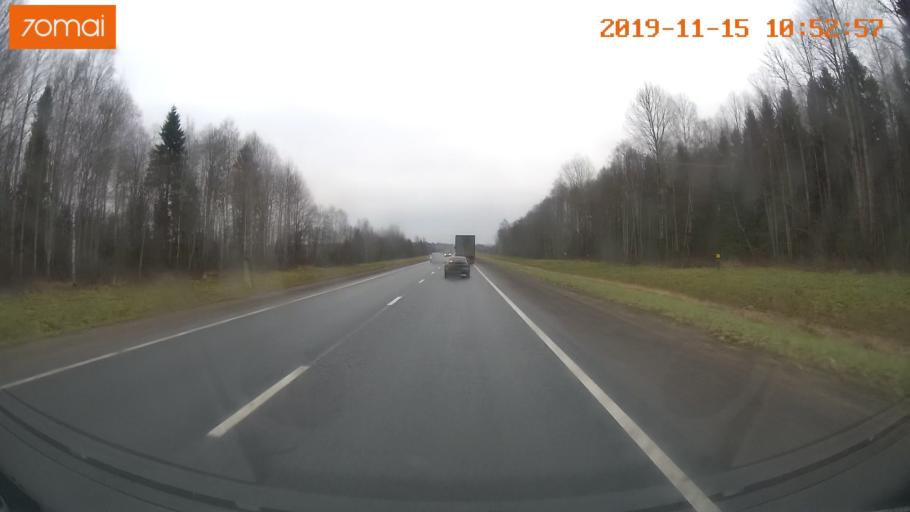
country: RU
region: Vologda
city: Chebsara
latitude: 59.1715
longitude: 38.7438
